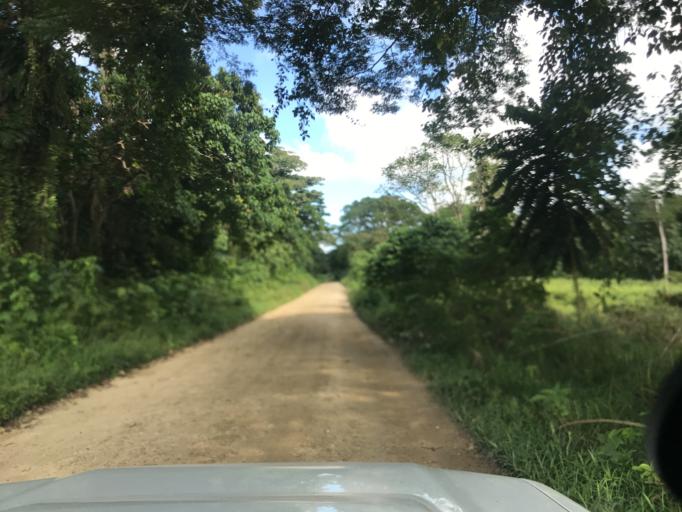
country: VU
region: Sanma
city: Luganville
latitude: -15.5098
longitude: 167.1227
